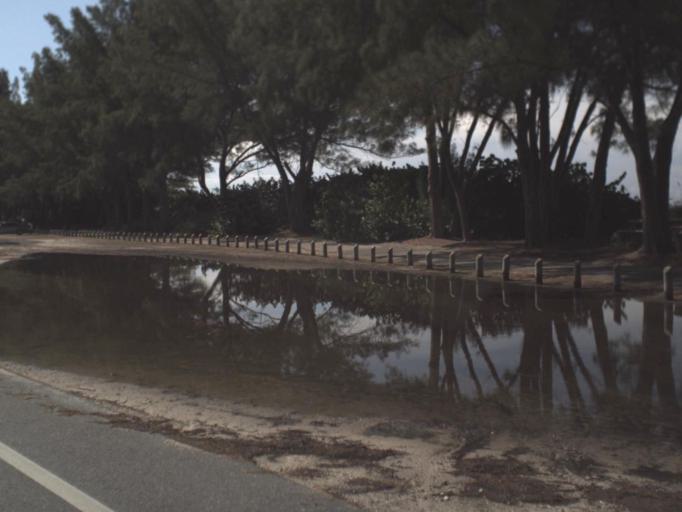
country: US
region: Florida
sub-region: Manatee County
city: Bradenton Beach
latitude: 27.4573
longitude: -82.6955
